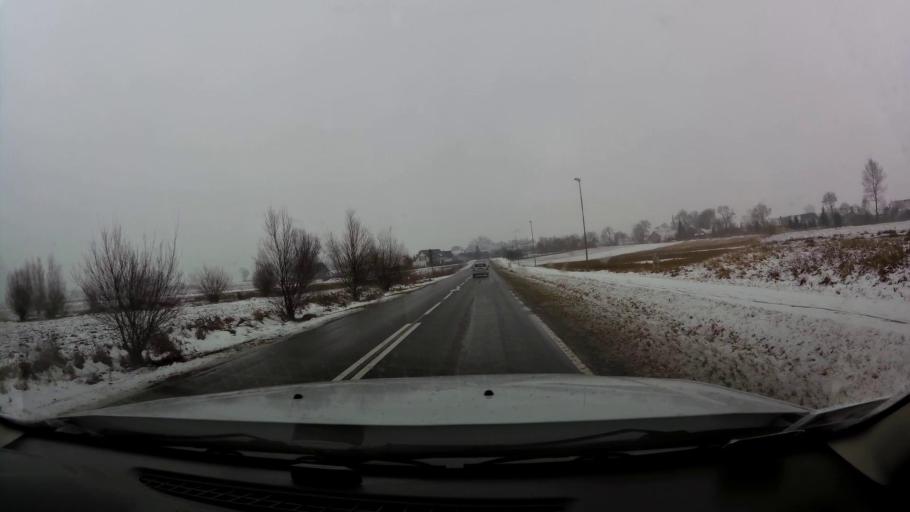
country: PL
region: West Pomeranian Voivodeship
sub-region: Powiat gryficki
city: Trzebiatow
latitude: 54.0950
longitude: 15.2664
